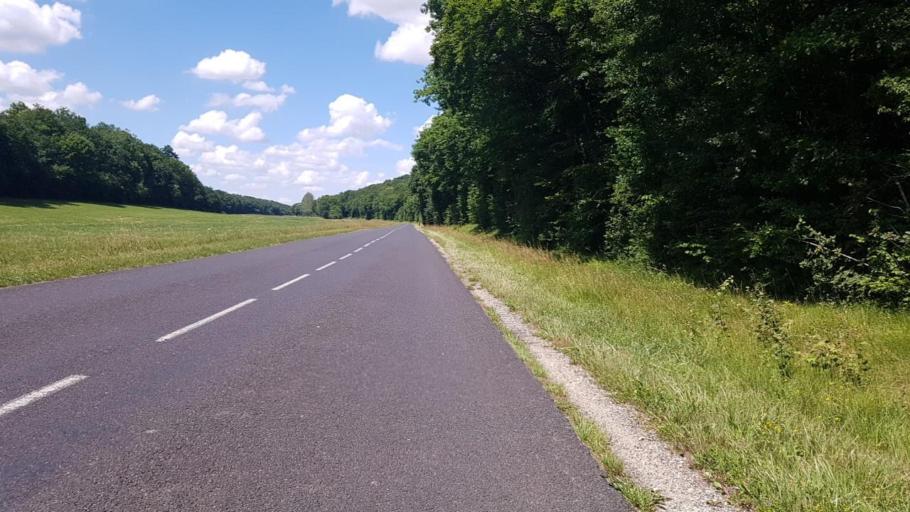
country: FR
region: Lorraine
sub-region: Departement de la Meuse
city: Vacon
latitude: 48.6726
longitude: 5.5834
